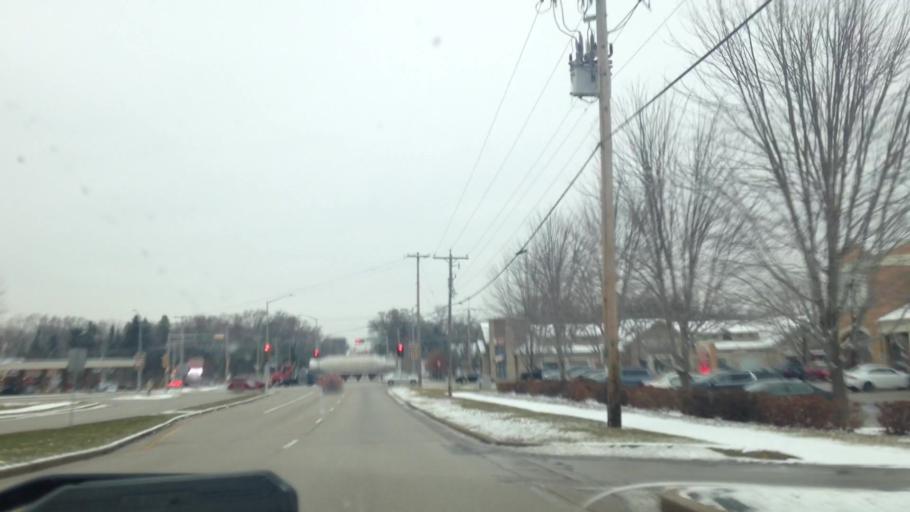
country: US
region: Wisconsin
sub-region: Waukesha County
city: Butler
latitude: 43.1181
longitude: -88.1052
